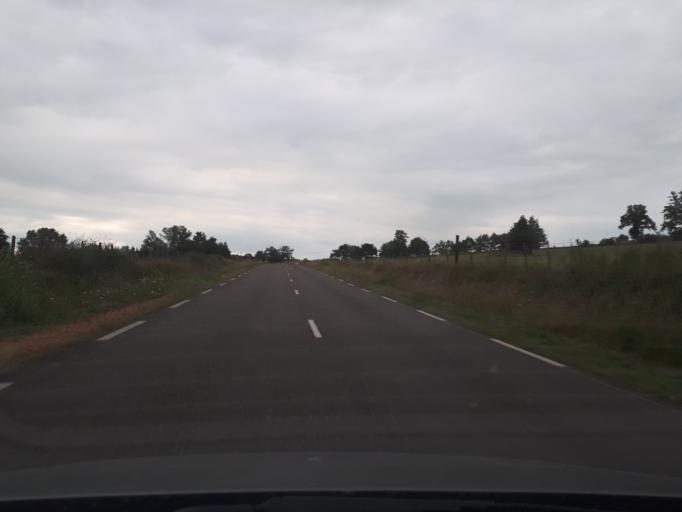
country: FR
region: Rhone-Alpes
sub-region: Departement de la Loire
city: Civens
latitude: 45.7476
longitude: 4.2738
